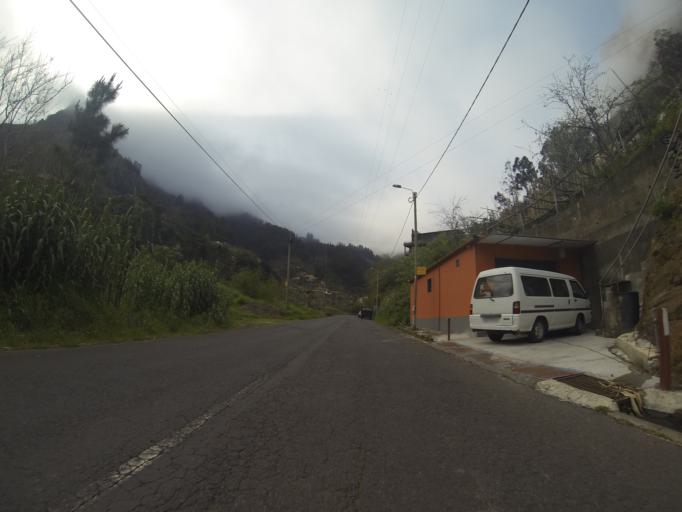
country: PT
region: Madeira
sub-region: Camara de Lobos
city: Curral das Freiras
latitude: 32.7372
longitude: -16.9688
